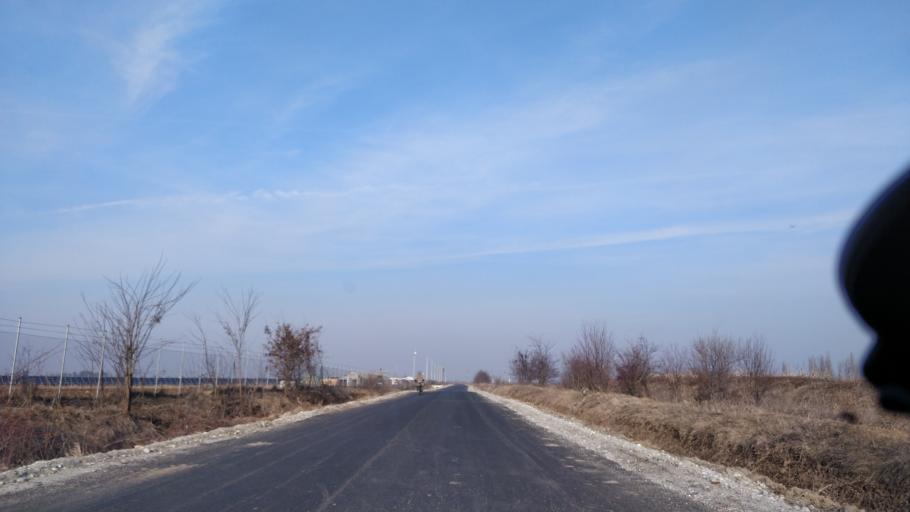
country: RO
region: Dambovita
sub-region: Comuna Brezoaiele
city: Brezoaia
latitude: 44.5351
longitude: 25.7959
